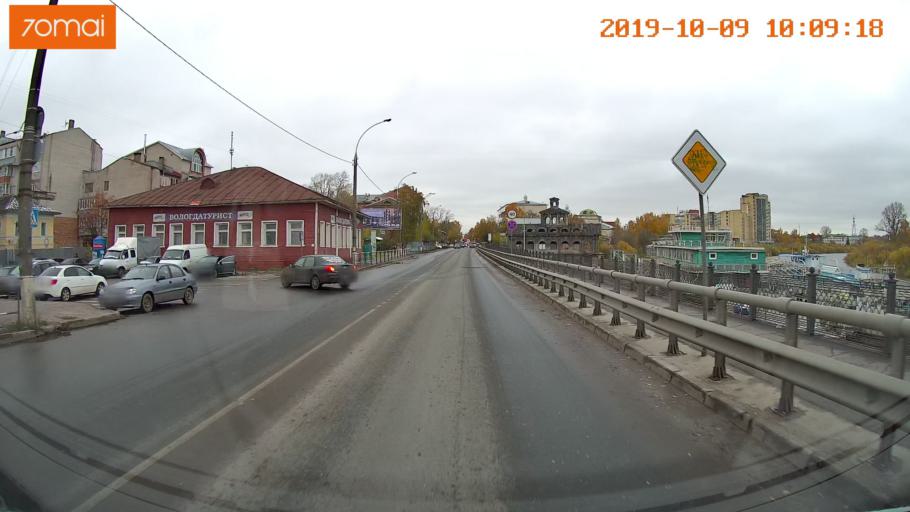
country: RU
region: Vologda
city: Vologda
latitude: 59.2110
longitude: 39.9053
